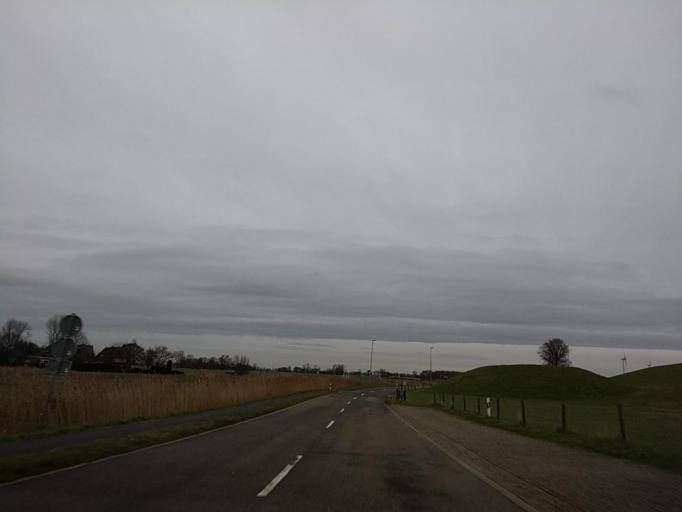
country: NL
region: Groningen
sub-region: Gemeente Delfzijl
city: Delfzijl
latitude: 53.3396
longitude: 7.0445
